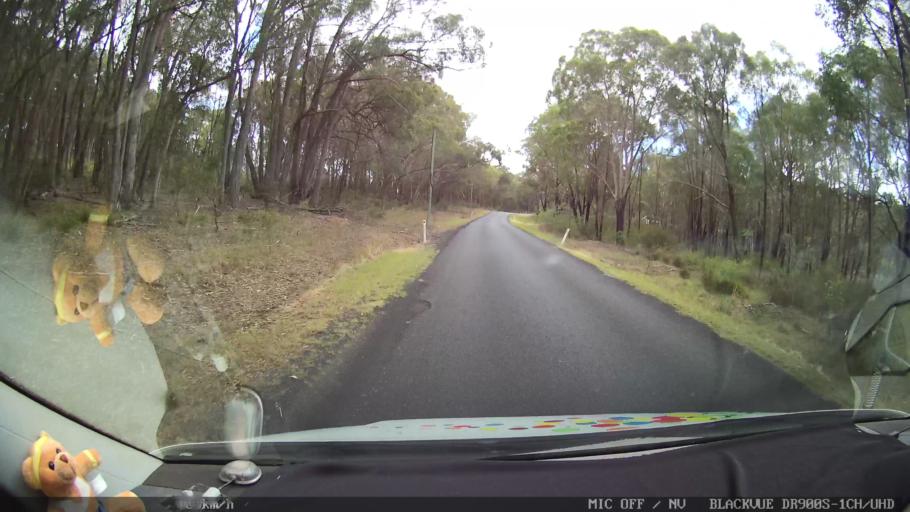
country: AU
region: New South Wales
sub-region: Glen Innes Severn
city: Glen Innes
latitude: -29.4338
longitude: 151.6329
